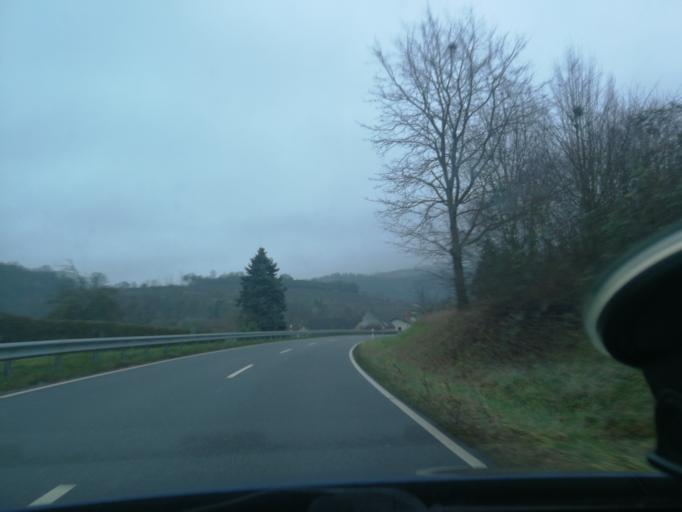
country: DE
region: Rheinland-Pfalz
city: Oberbillig
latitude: 49.7235
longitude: 6.5018
